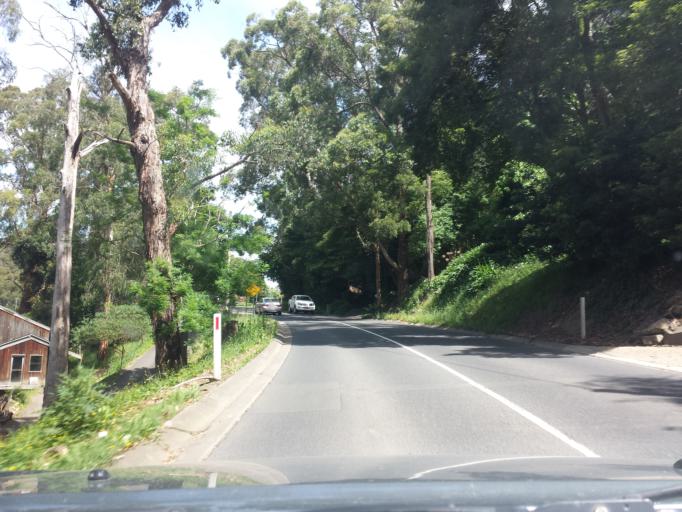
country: AU
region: Victoria
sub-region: Yarra Ranges
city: Belgrave Heights
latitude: -37.9121
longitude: 145.3614
